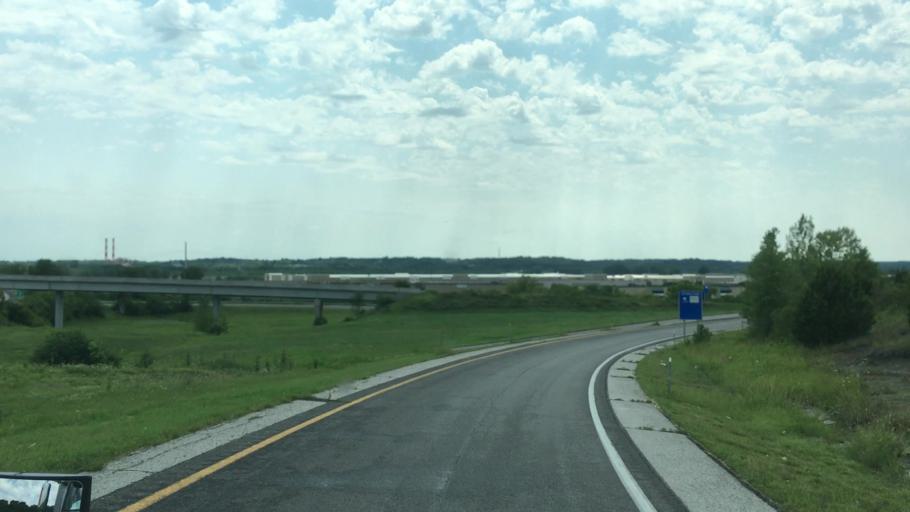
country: US
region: Missouri
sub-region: Platte County
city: Riverside
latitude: 39.1739
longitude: -94.6236
